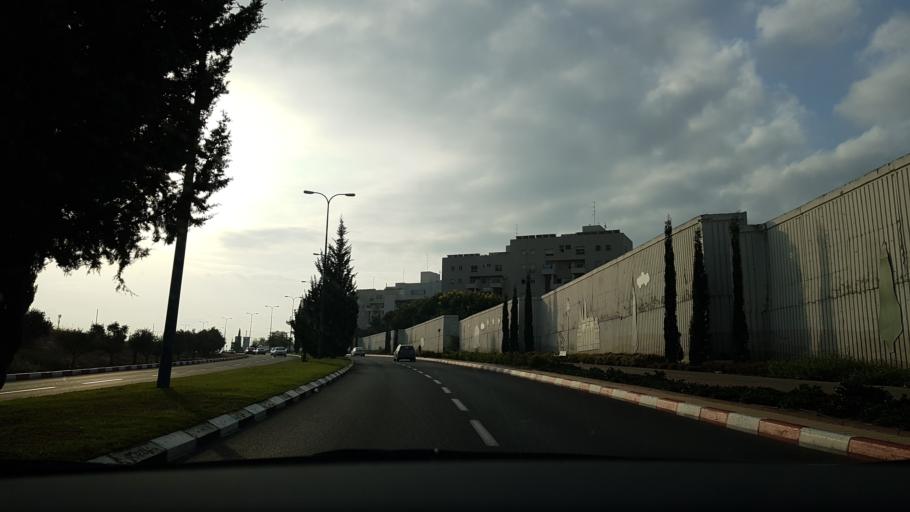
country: IL
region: Central District
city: Mazkeret Batya
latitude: 31.8929
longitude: 34.8282
